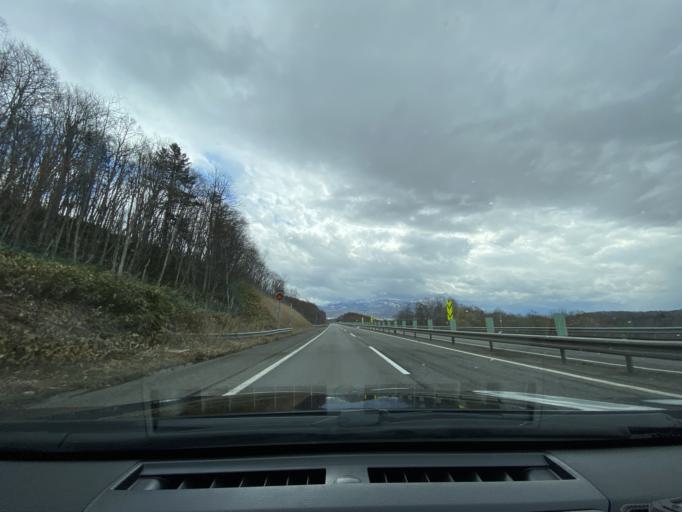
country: JP
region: Hokkaido
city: Fukagawa
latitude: 43.7599
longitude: 142.1694
